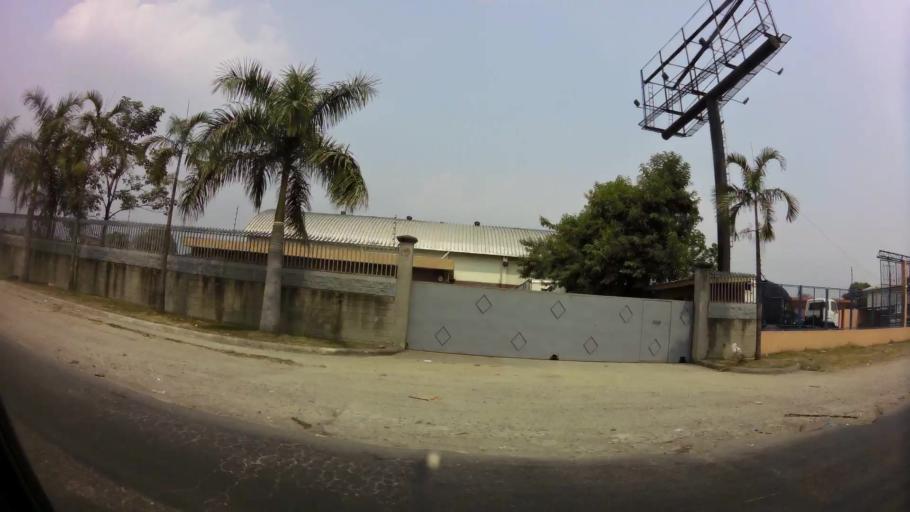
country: HN
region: Cortes
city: San Pedro Sula
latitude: 15.4802
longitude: -88.0077
